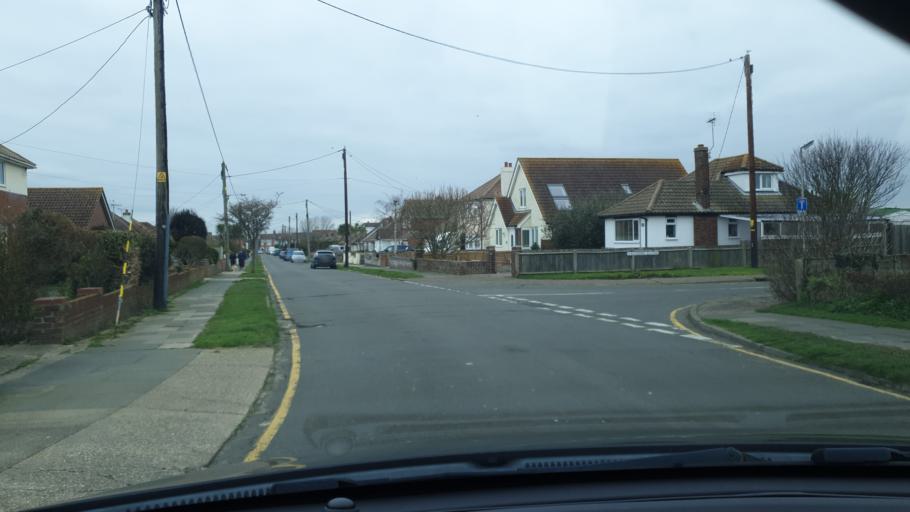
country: GB
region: England
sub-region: Essex
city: Walton-on-the-Naze
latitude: 51.8579
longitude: 1.2827
